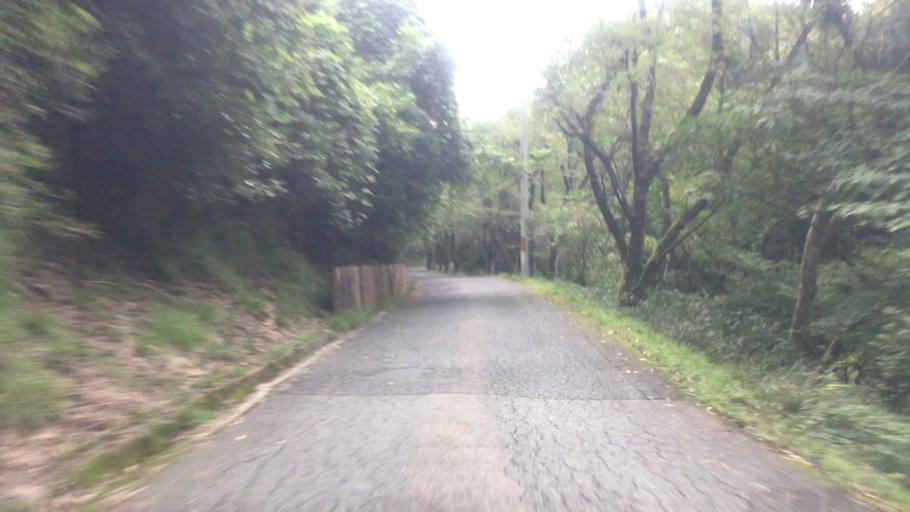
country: JP
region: Hyogo
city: Toyooka
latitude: 35.6217
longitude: 134.8769
